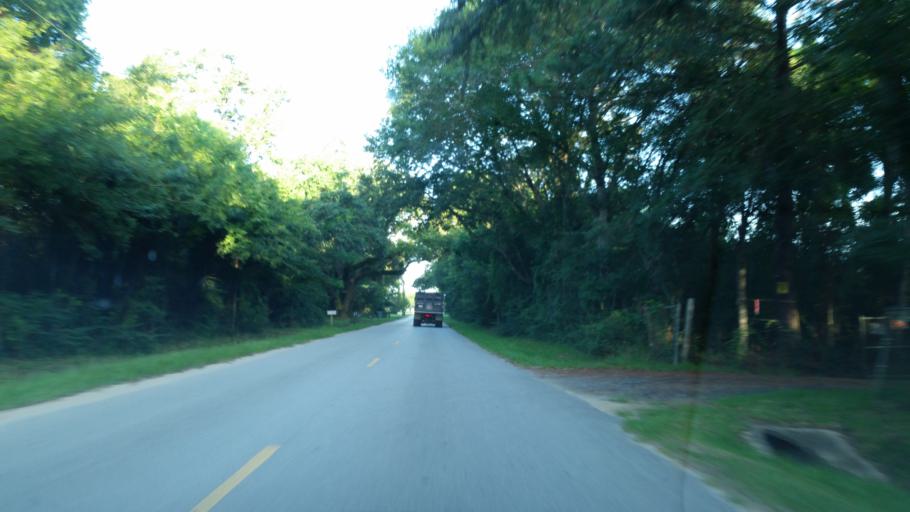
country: US
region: Florida
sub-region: Escambia County
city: Bellview
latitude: 30.4691
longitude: -87.3287
